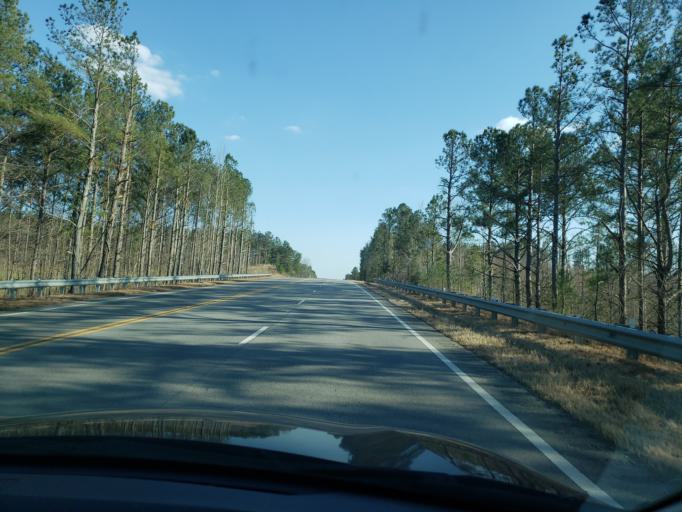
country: US
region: Alabama
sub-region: Randolph County
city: Wedowee
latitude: 33.4461
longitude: -85.5690
